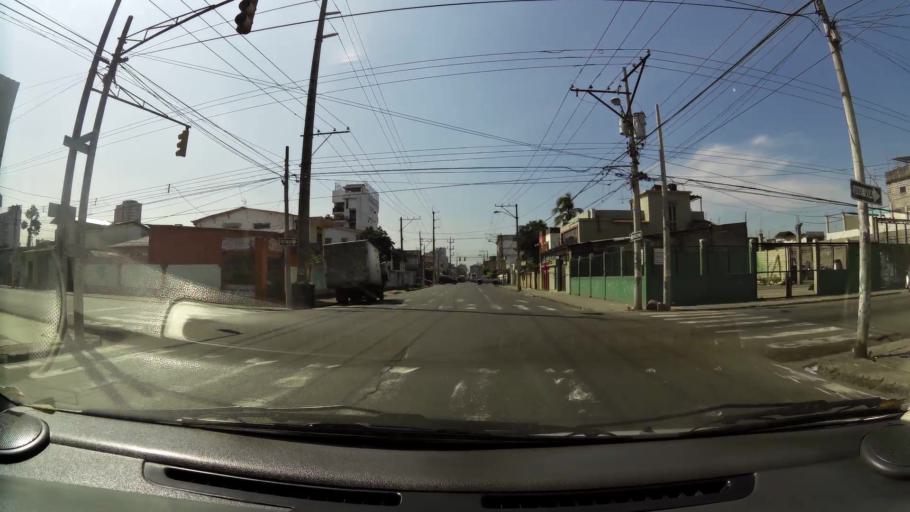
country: EC
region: Guayas
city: Guayaquil
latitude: -2.1911
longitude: -79.8982
